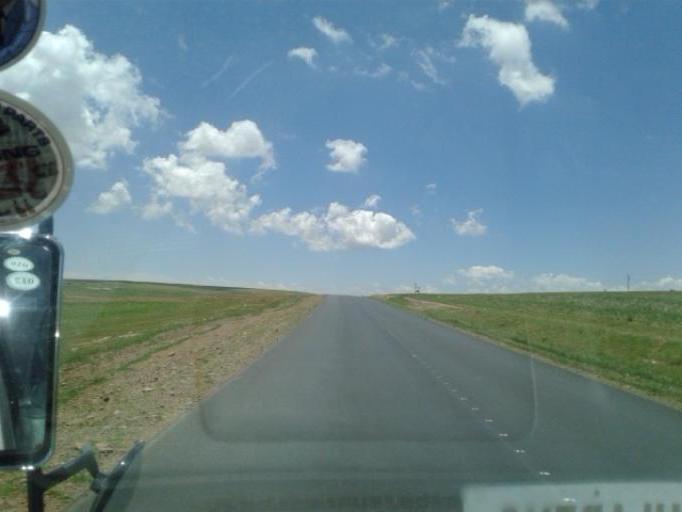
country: LS
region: Maseru
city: Maseru
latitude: -29.3095
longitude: 27.6006
